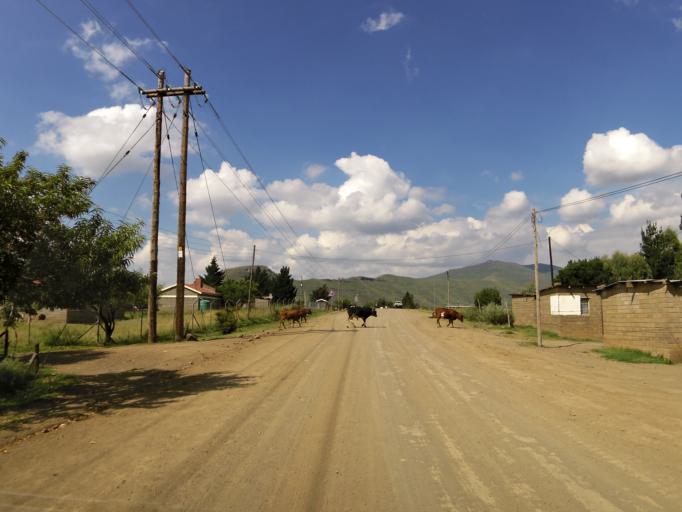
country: LS
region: Butha-Buthe
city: Butha-Buthe
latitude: -29.1067
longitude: 28.4953
